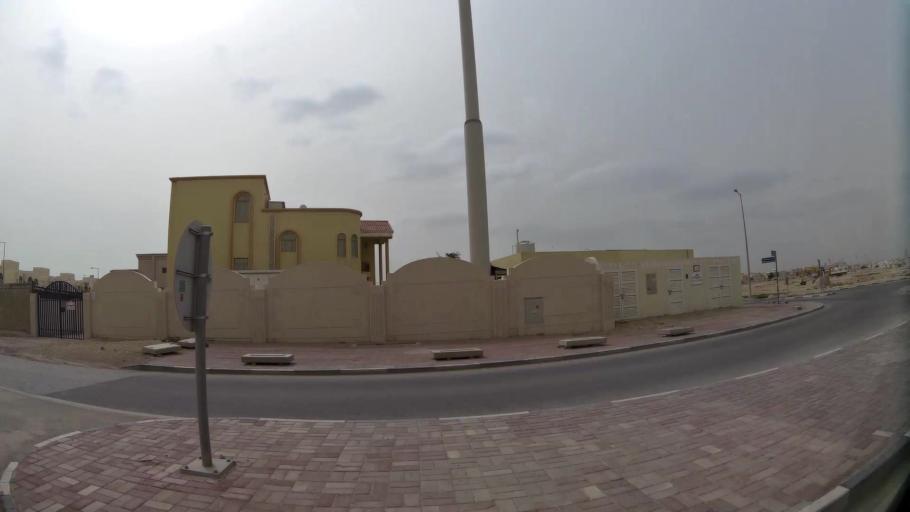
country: QA
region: Baladiyat ad Dawhah
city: Doha
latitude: 25.2395
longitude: 51.5289
